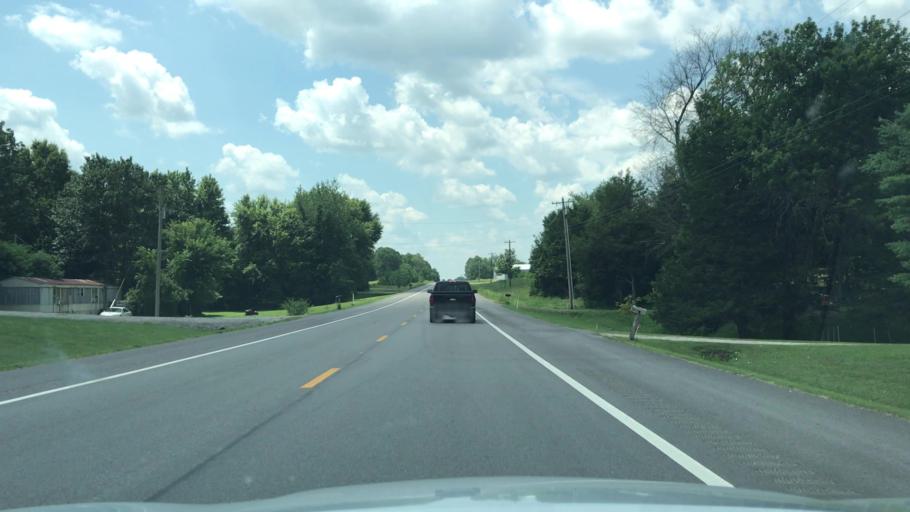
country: US
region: Tennessee
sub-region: Pickett County
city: Byrdstown
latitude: 36.5139
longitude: -85.1709
